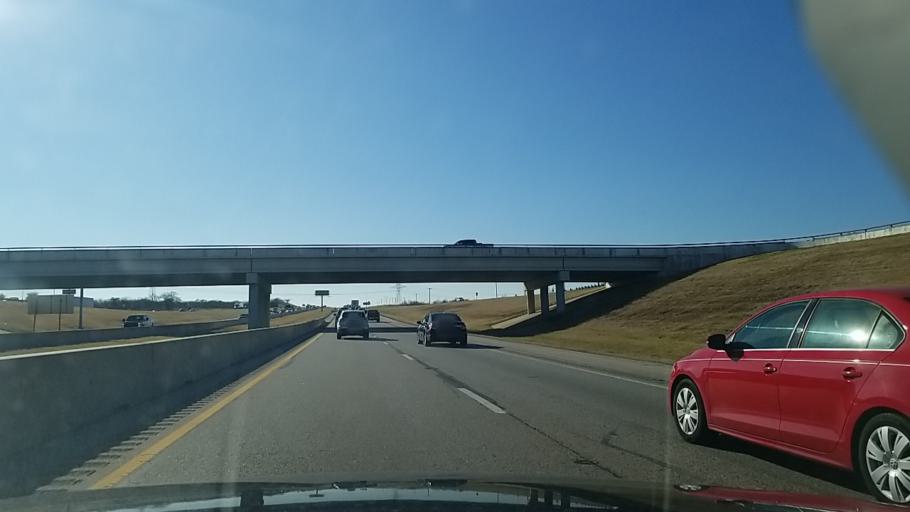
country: US
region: Texas
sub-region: Tarrant County
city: Haslet
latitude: 32.9592
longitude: -97.3106
